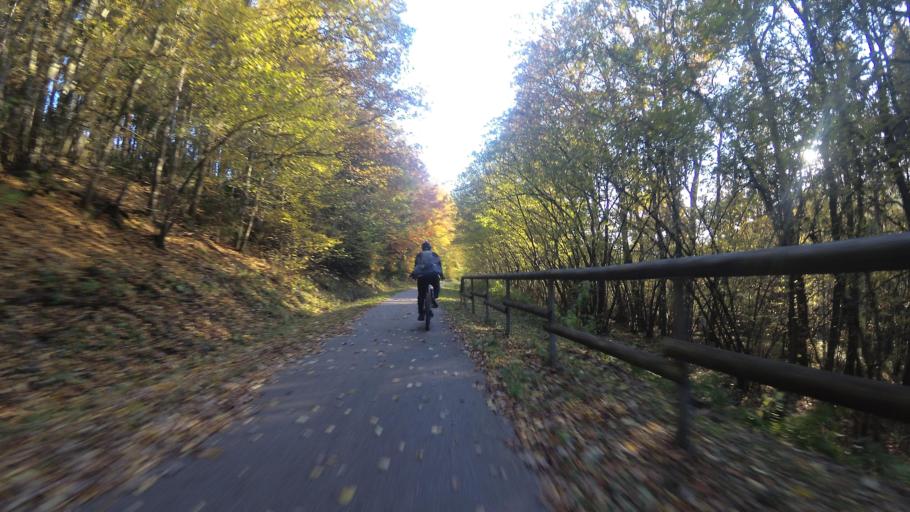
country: DE
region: Rheinland-Pfalz
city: Schomerich
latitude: 49.6363
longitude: 6.7197
